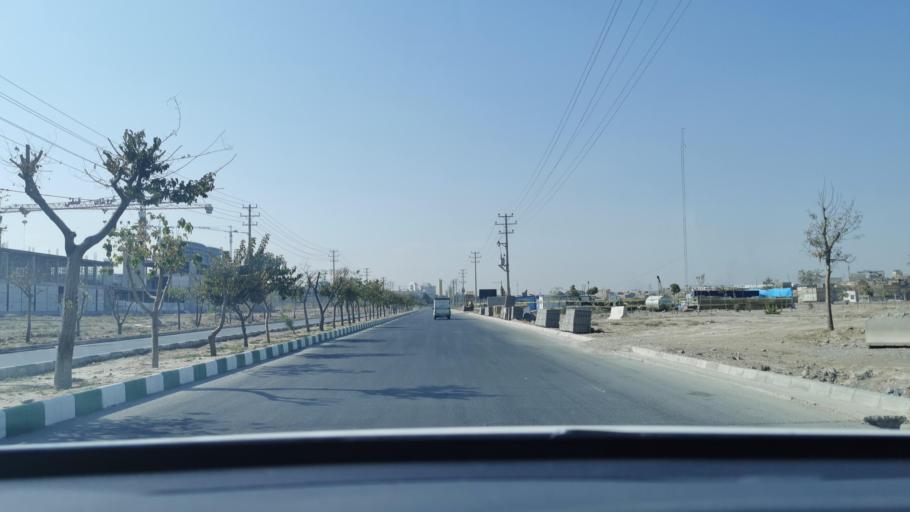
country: IR
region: Razavi Khorasan
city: Mashhad
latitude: 36.3480
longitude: 59.6097
